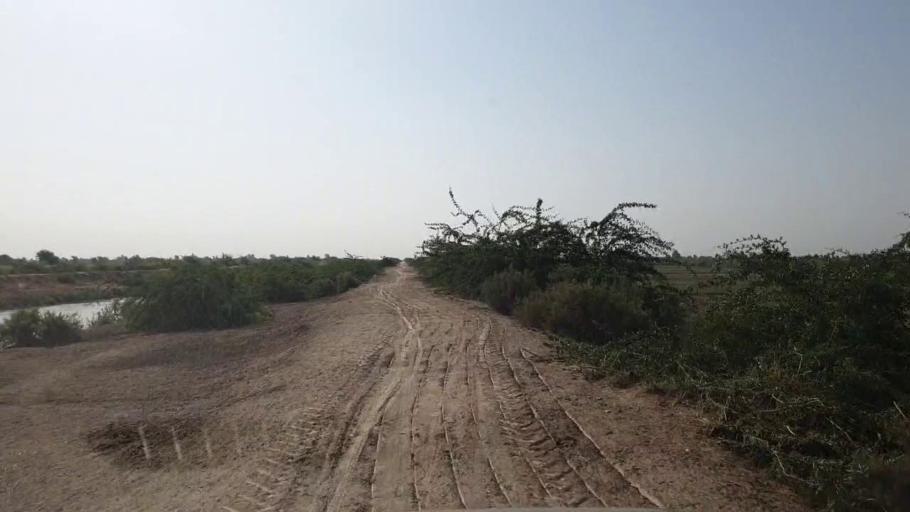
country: PK
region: Sindh
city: Kadhan
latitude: 24.5831
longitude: 69.0790
